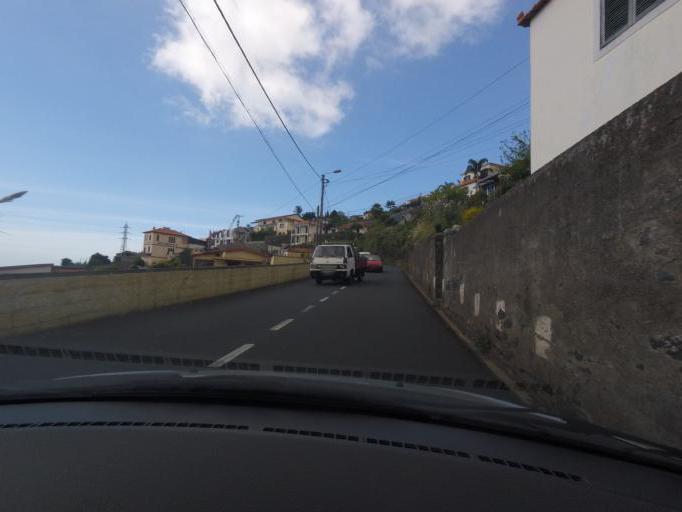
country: PT
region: Madeira
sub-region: Funchal
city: Nossa Senhora do Monte
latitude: 32.6718
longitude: -16.9414
